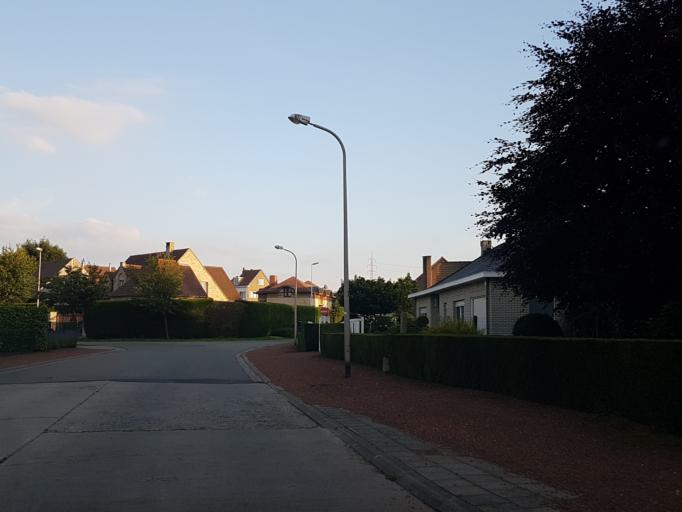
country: BE
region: Flanders
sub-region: Provincie Vlaams-Brabant
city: Dilbeek
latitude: 50.8512
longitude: 4.2362
